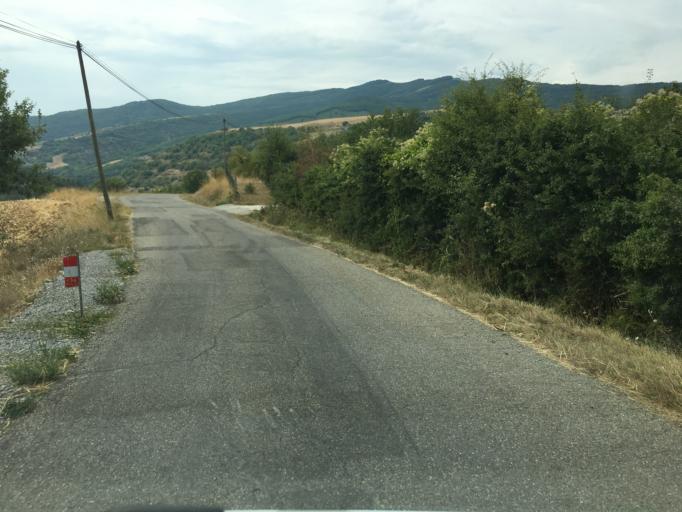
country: FR
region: Provence-Alpes-Cote d'Azur
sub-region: Departement des Alpes-de-Haute-Provence
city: Digne-les-Bains
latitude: 44.1876
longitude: 6.1416
